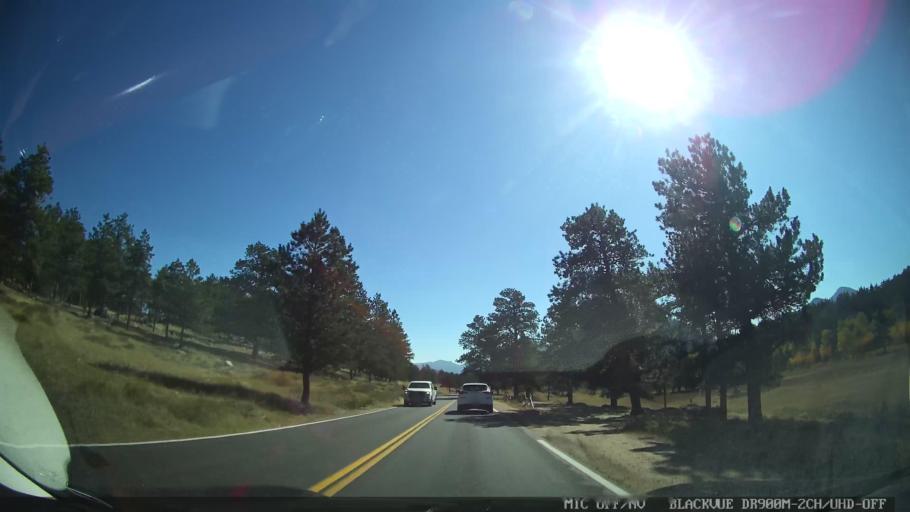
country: US
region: Colorado
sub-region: Larimer County
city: Estes Park
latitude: 40.3674
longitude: -105.5895
